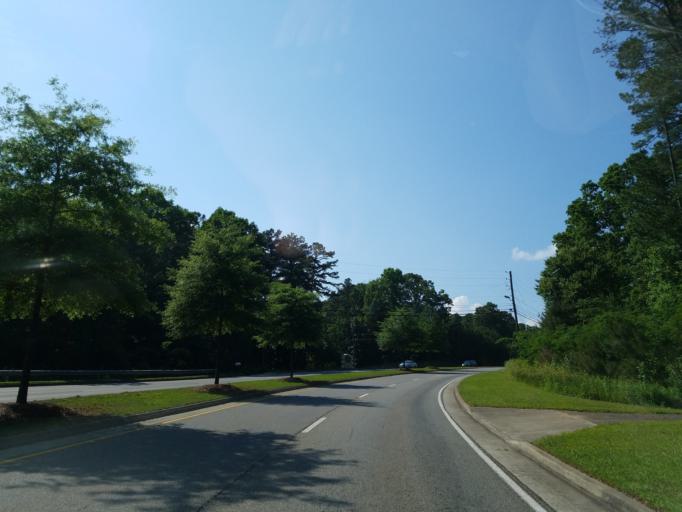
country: US
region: Georgia
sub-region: Cherokee County
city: Holly Springs
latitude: 34.1542
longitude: -84.5245
